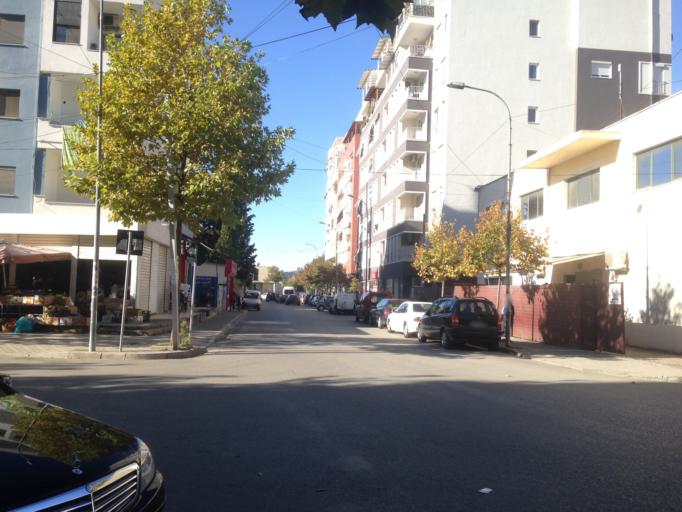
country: AL
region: Tirane
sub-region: Rrethi i Tiranes
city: Paskuqan
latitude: 41.3394
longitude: 19.8046
